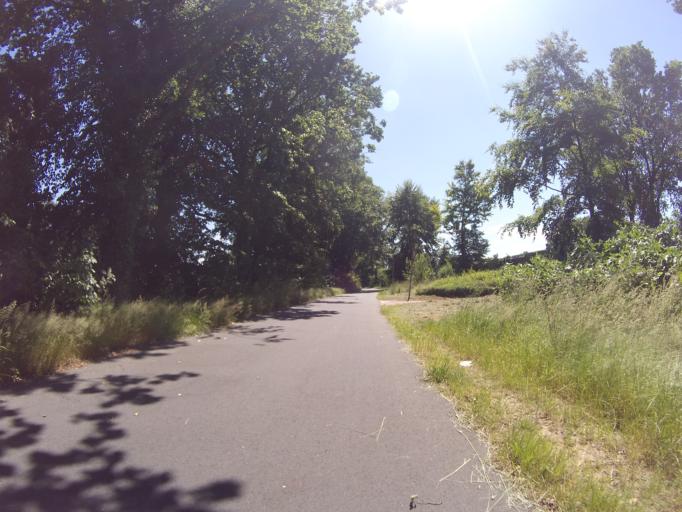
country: NL
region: Drenthe
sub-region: Gemeente Emmen
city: Emmen
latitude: 52.7948
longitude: 6.9494
